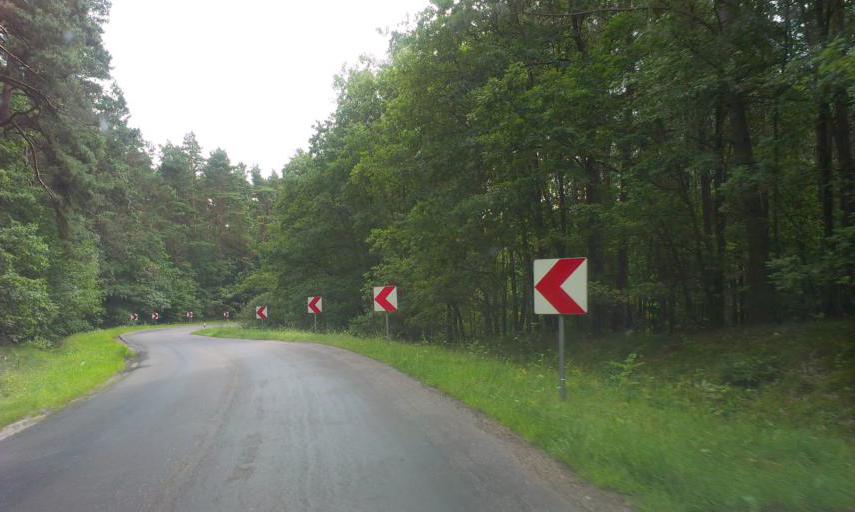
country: PL
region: West Pomeranian Voivodeship
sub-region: Powiat swidwinski
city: Polczyn-Zdroj
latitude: 53.7788
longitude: 16.1479
